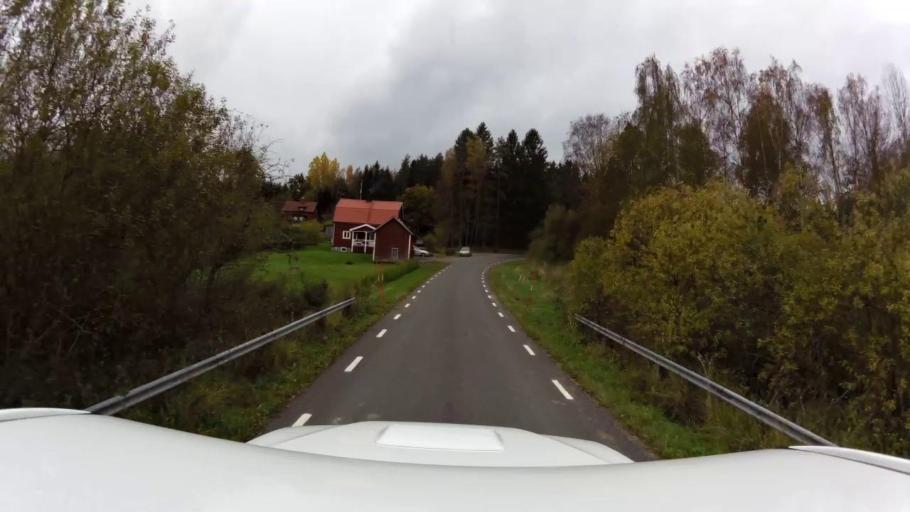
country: SE
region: OEstergoetland
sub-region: Linkopings Kommun
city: Ljungsbro
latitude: 58.5693
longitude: 15.4589
